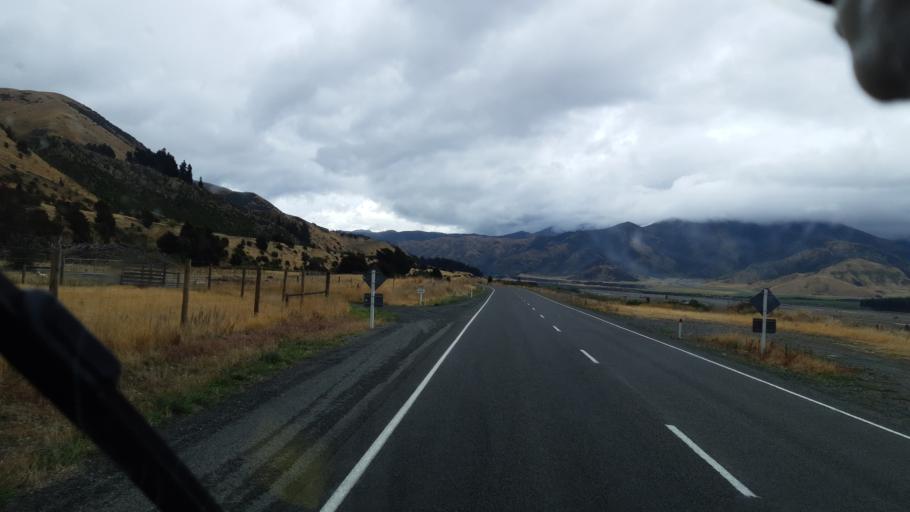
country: NZ
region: Canterbury
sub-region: Hurunui District
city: Amberley
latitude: -42.5764
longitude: 172.7289
